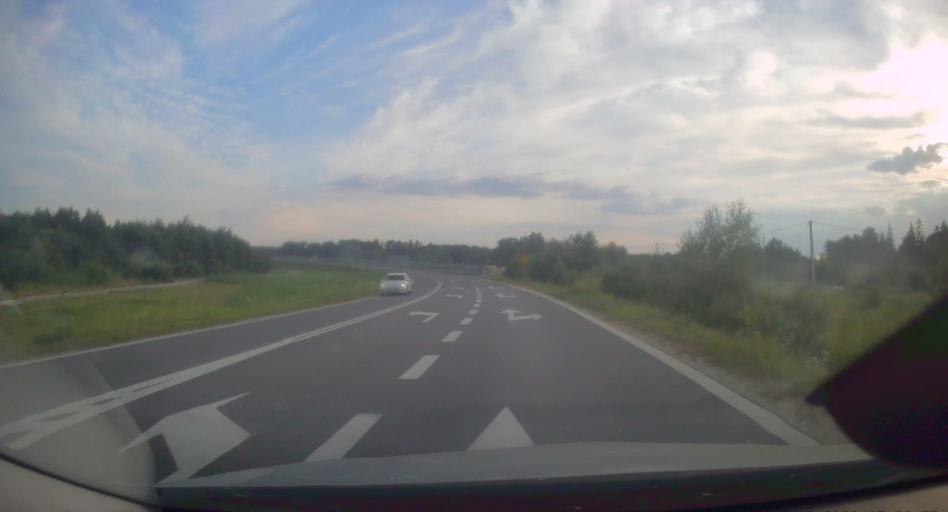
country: PL
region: Lesser Poland Voivodeship
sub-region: Powiat brzeski
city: Brzesko
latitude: 49.9965
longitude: 20.5926
